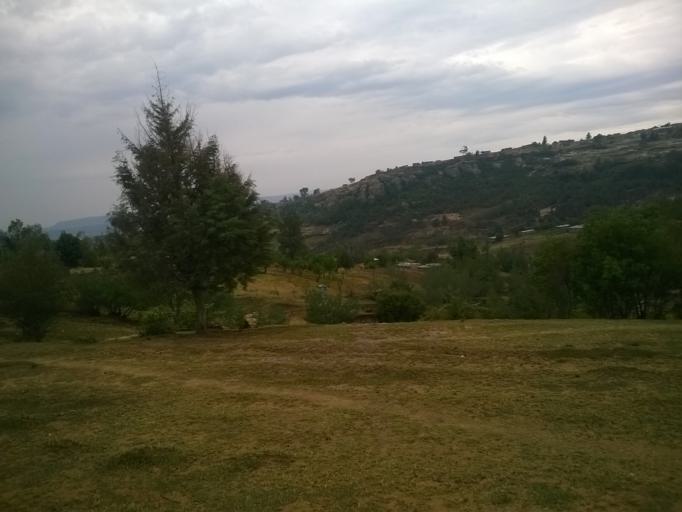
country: LS
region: Berea
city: Teyateyaneng
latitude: -29.1402
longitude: 27.7396
